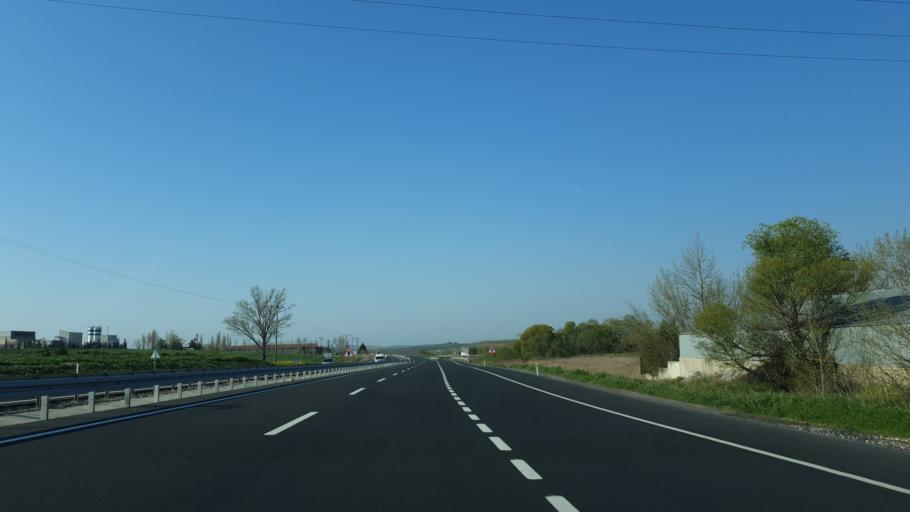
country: TR
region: Tekirdag
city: Corlu
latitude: 41.1240
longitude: 27.7536
